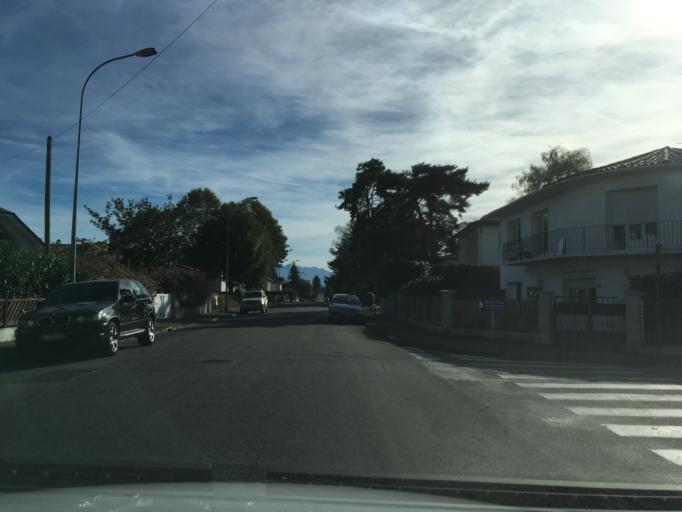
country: FR
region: Aquitaine
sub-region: Departement des Pyrenees-Atlantiques
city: Lons
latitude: 43.3325
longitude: -0.3739
